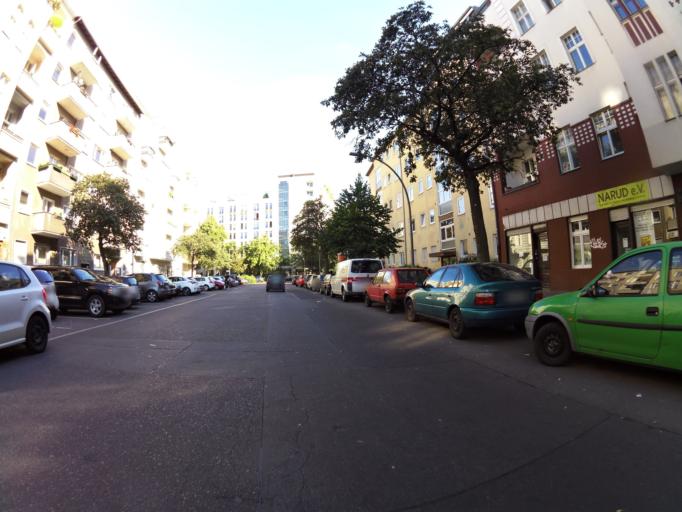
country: DE
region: Berlin
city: Wedding Bezirk
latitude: 52.5444
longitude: 13.3582
